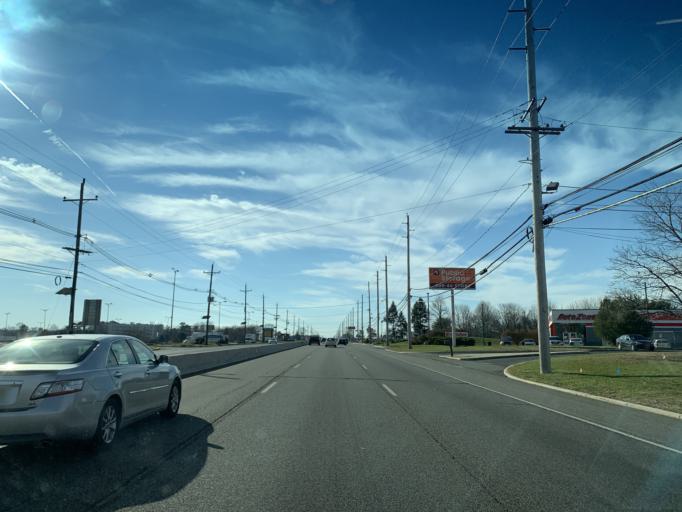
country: US
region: New Jersey
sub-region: Burlington County
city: Edgewater Park
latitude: 40.0516
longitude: -74.8959
